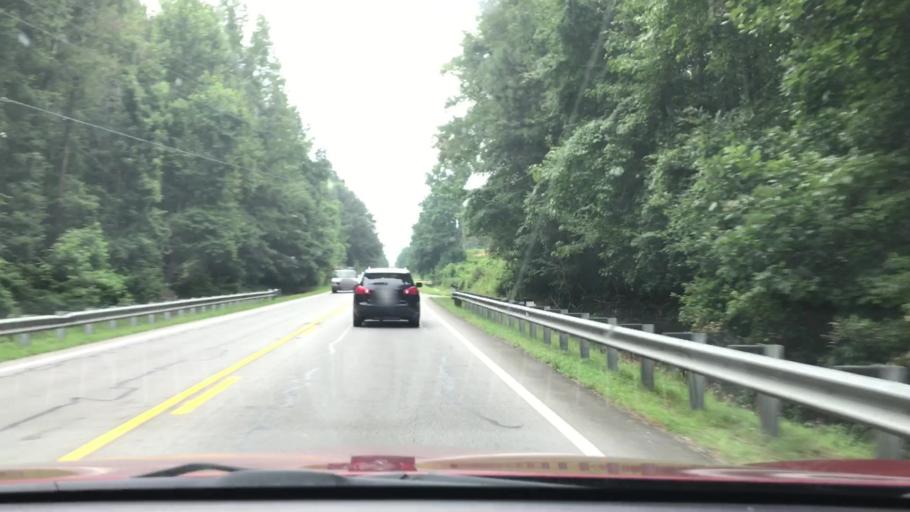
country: US
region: Georgia
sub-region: Jackson County
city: Hoschton
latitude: 34.0778
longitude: -83.7917
